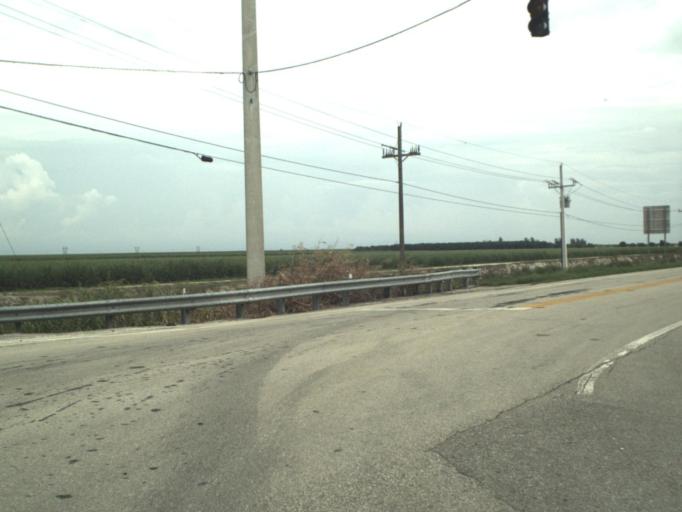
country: US
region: Florida
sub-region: Palm Beach County
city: Belle Glade
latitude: 26.7258
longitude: -80.6840
